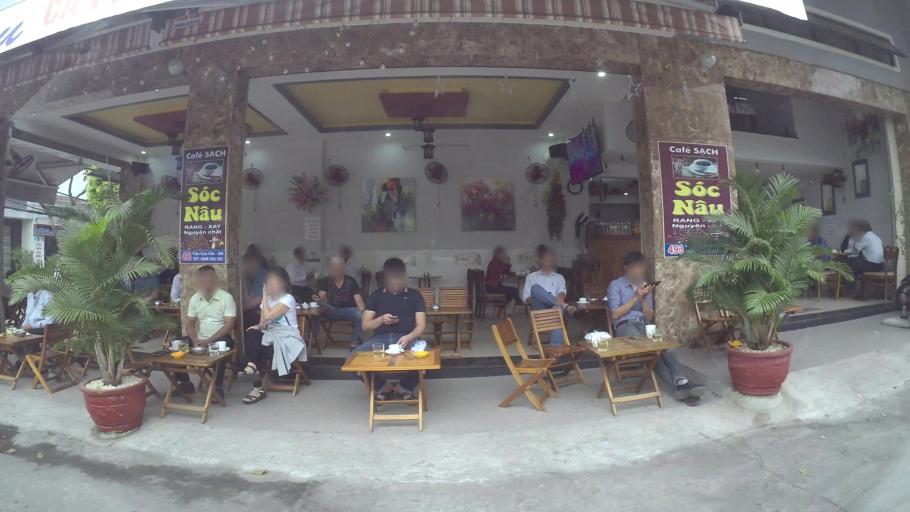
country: VN
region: Da Nang
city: Thanh Khe
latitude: 16.0711
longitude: 108.1926
